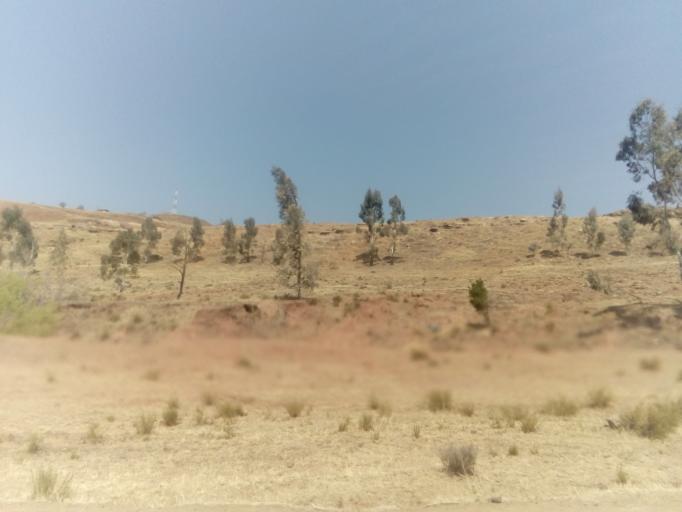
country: LS
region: Leribe
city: Leribe
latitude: -29.1324
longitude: 28.0693
